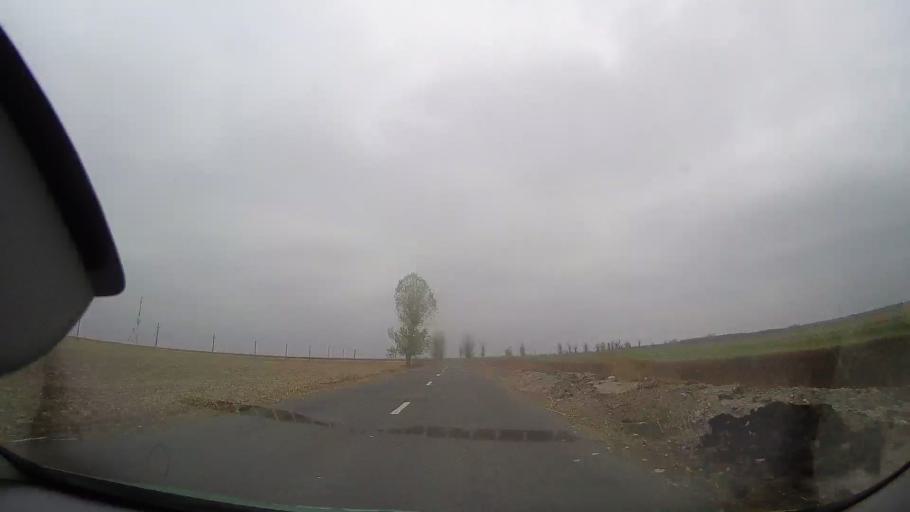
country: RO
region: Ialomita
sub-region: Comuna Grindu
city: Grindu
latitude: 44.7939
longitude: 26.8942
